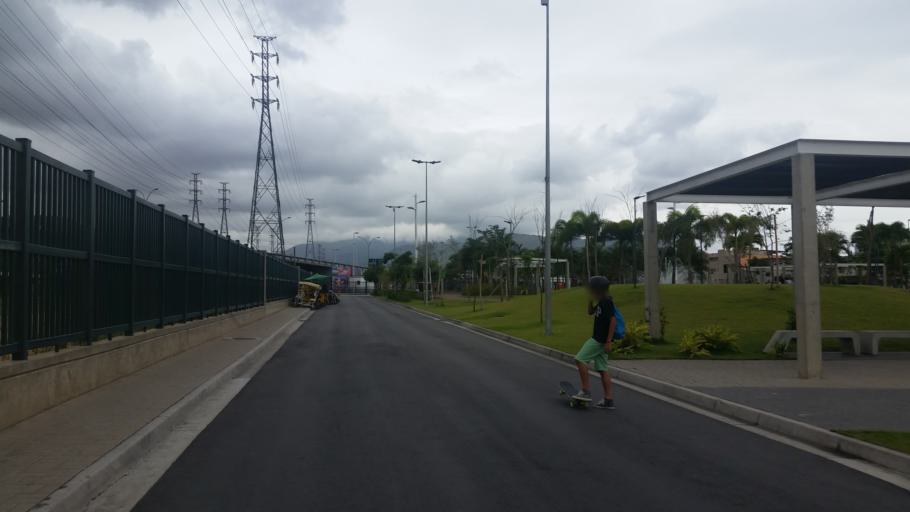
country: BR
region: Rio de Janeiro
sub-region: Sao Joao De Meriti
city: Sao Joao de Meriti
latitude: -22.8588
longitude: -43.3491
